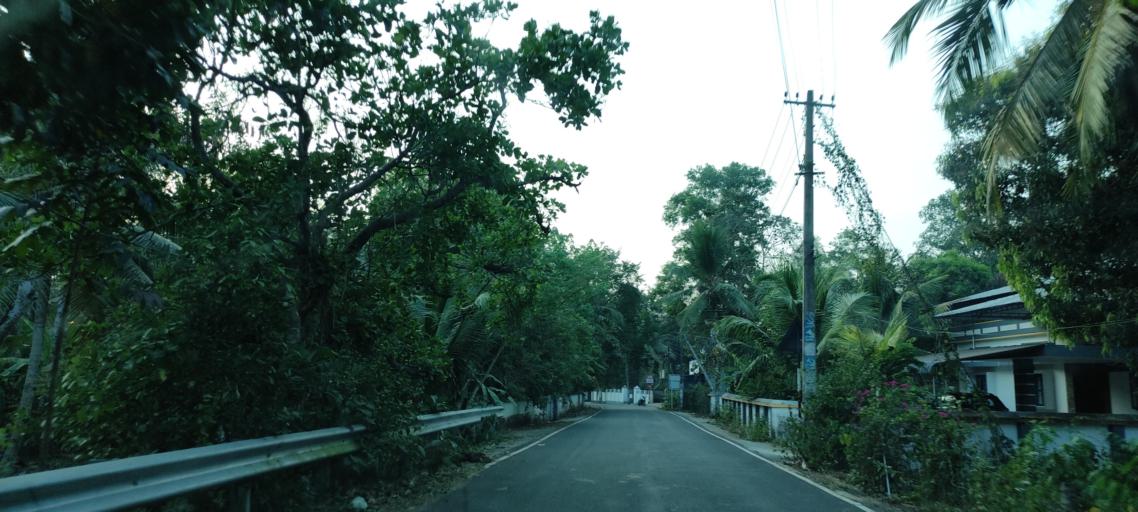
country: IN
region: Kerala
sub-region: Alappuzha
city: Mavelikara
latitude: 9.2773
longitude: 76.5592
